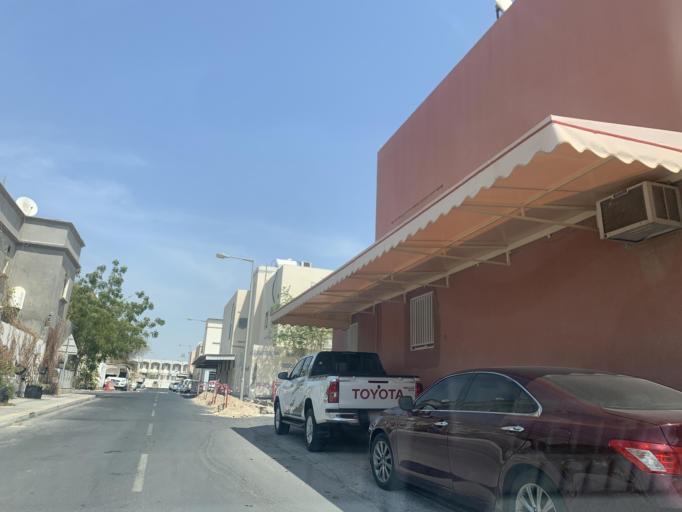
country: BH
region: Central Governorate
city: Madinat Hamad
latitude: 26.1346
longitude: 50.5021
